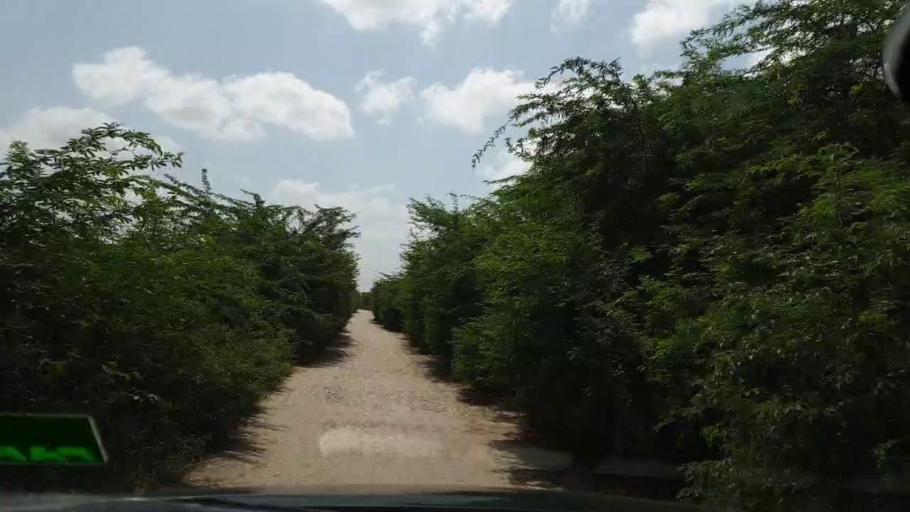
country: PK
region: Sindh
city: Kadhan
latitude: 24.5652
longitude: 69.2110
